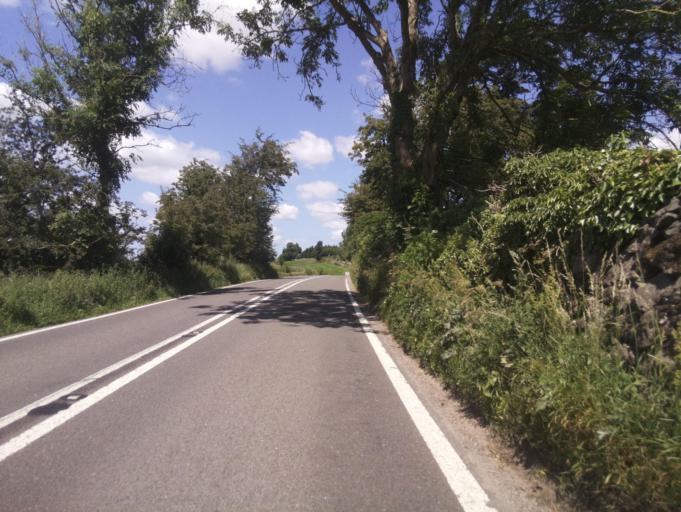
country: GB
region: England
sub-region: Derbyshire
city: Ashbourne
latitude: 53.0672
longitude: -1.7480
